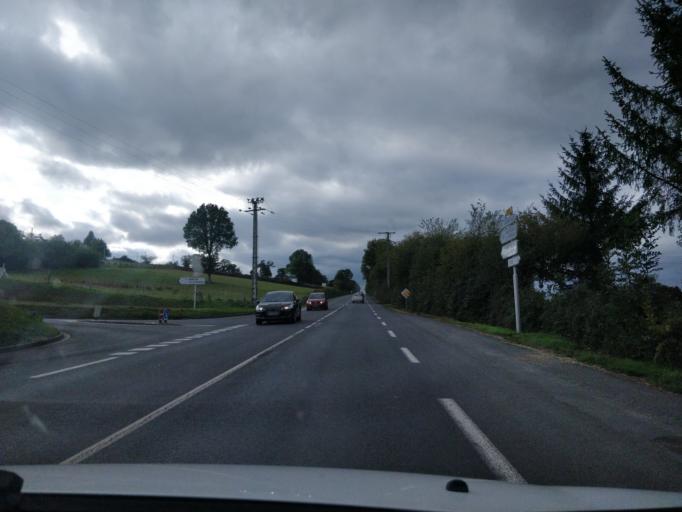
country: FR
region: Lower Normandy
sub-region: Departement du Calvados
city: Vire
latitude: 48.8447
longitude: -0.9134
